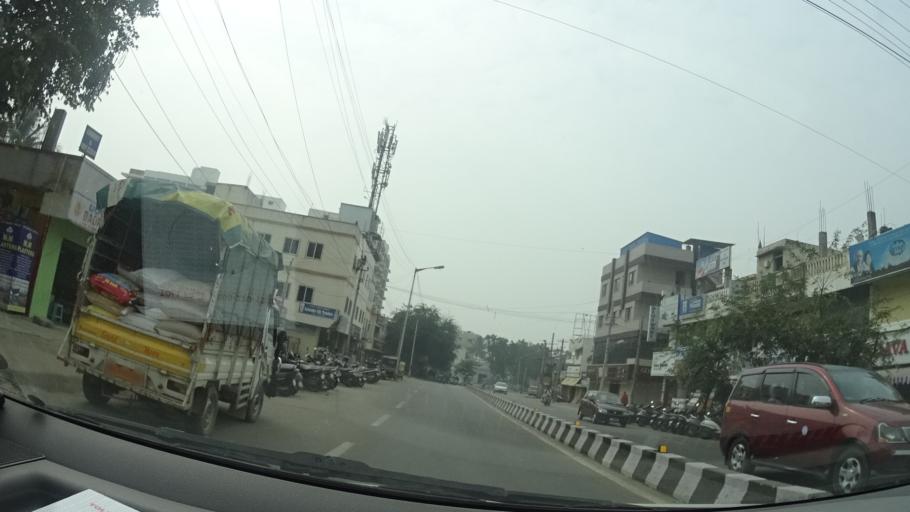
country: IN
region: Karnataka
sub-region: Bangalore Urban
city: Bangalore
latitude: 13.0252
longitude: 77.6306
